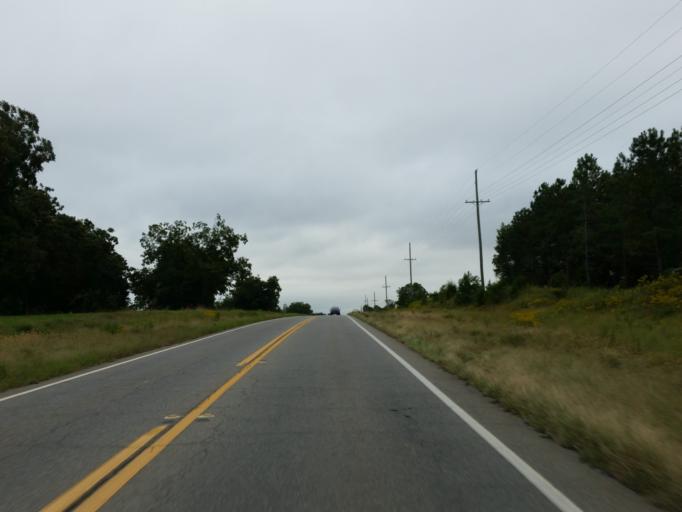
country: US
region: Georgia
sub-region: Houston County
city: Perry
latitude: 32.4846
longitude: -83.7760
